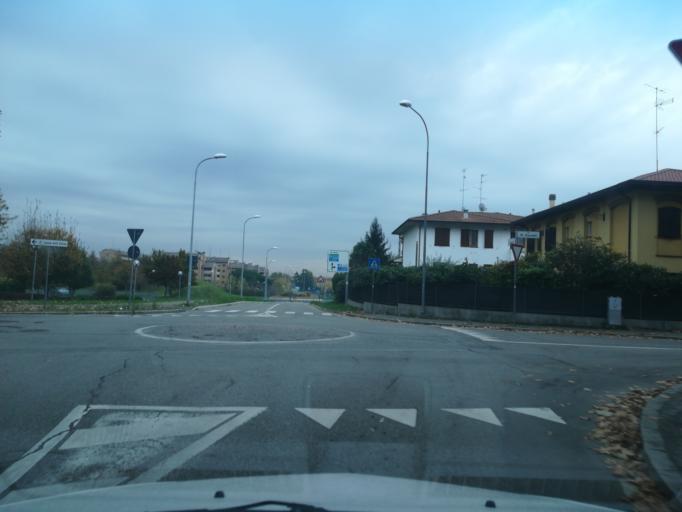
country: IT
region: Emilia-Romagna
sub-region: Provincia di Bologna
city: Imola
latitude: 44.3649
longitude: 11.6959
